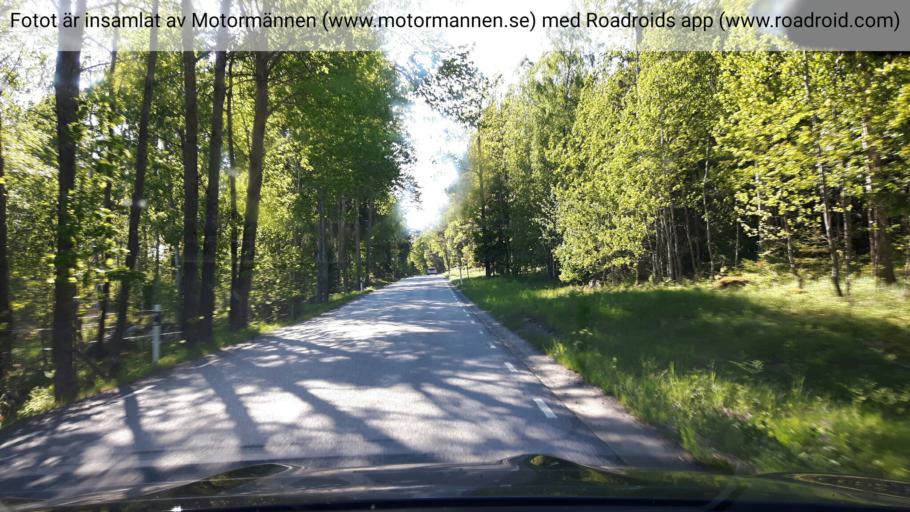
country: SE
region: Stockholm
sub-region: Norrtalje Kommun
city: Norrtalje
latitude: 59.6670
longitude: 18.8491
